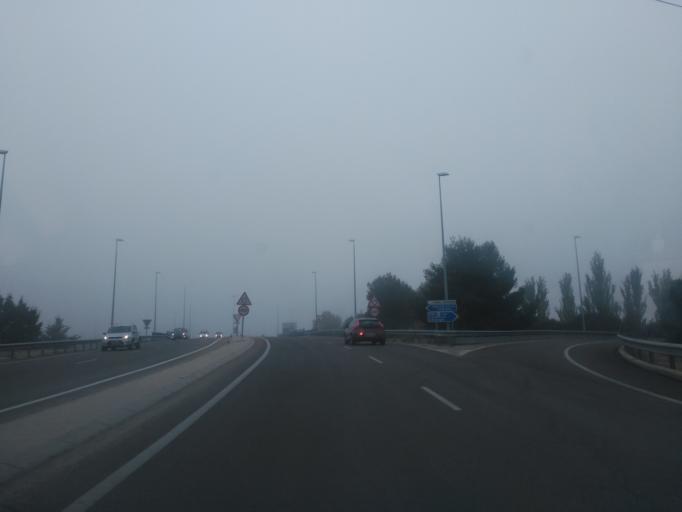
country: ES
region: Castille and Leon
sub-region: Provincia de Valladolid
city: Zaratan
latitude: 41.6344
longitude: -4.7747
